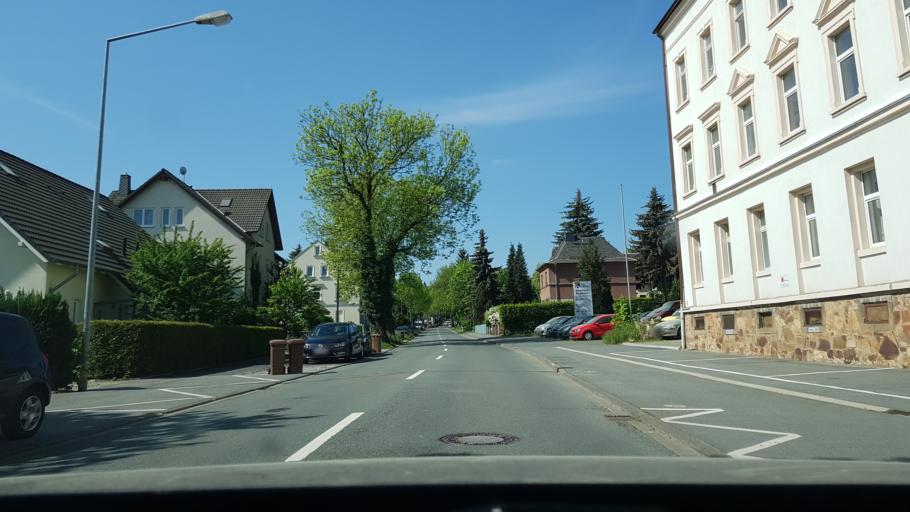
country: DE
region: Saxony
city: Wittgensdorf
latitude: 50.8591
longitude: 12.8894
